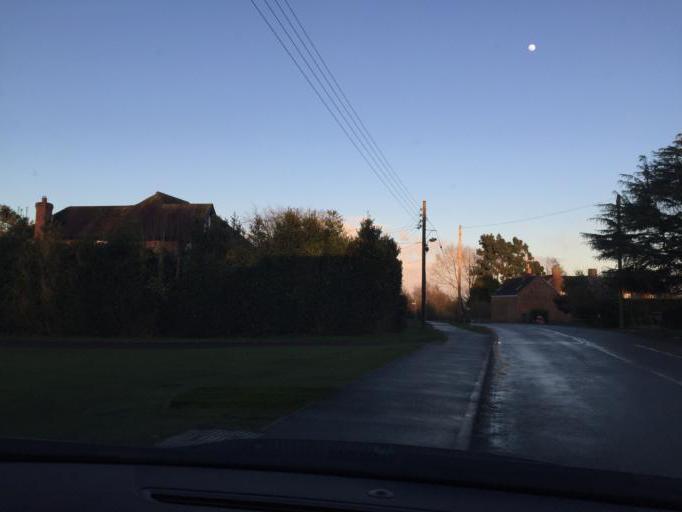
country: GB
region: England
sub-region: Warwickshire
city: Wroxall
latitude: 52.2676
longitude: -1.6719
